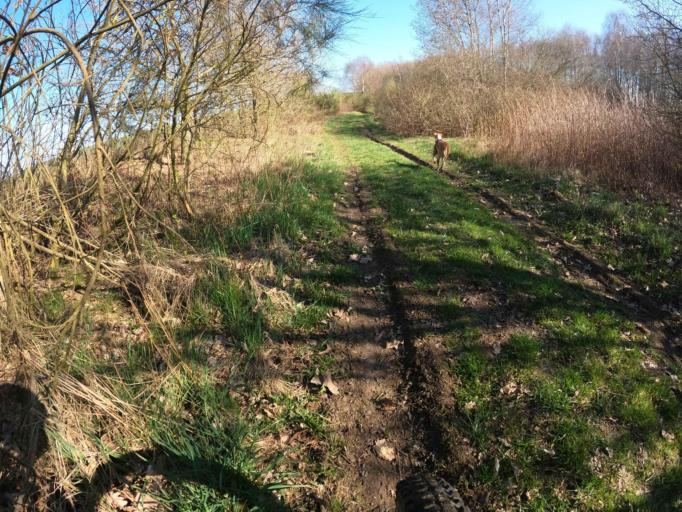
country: PL
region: West Pomeranian Voivodeship
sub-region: Powiat kolobrzeski
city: Ryman
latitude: 54.0114
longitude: 15.4804
